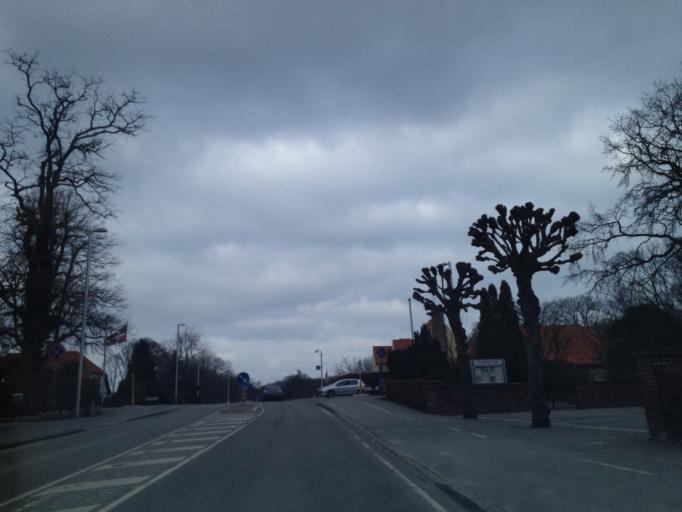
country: DK
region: Capital Region
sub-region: Fredensborg Kommune
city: Humlebaek
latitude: 55.9715
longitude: 12.5415
